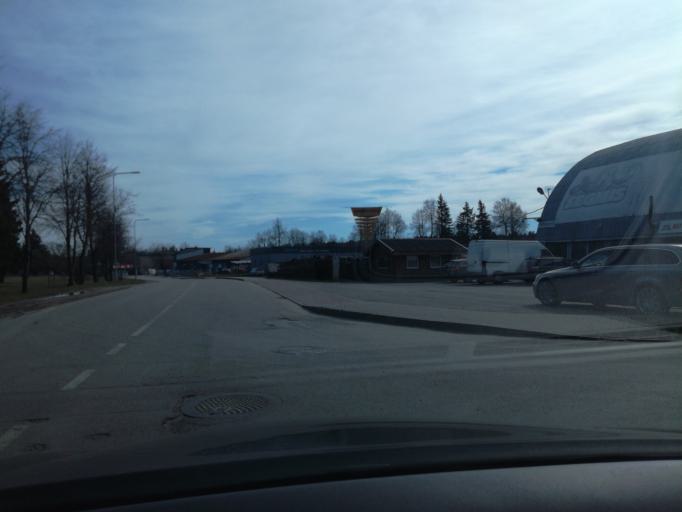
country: LT
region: Alytaus apskritis
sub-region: Alytus
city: Alytus
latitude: 54.3906
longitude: 24.0377
